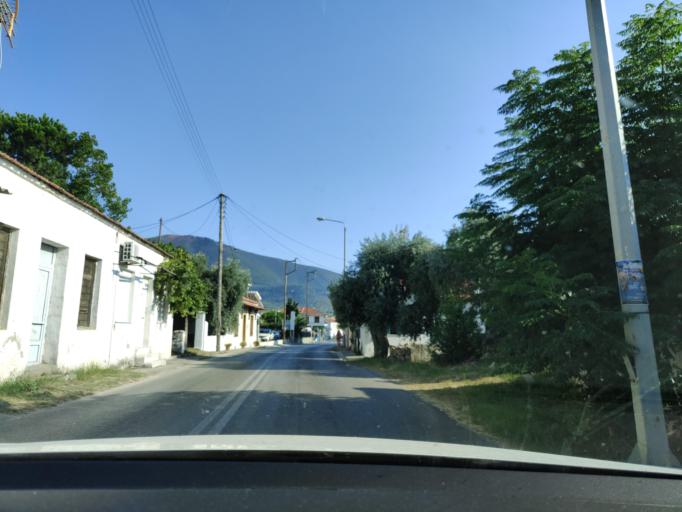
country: GR
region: East Macedonia and Thrace
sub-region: Nomos Kavalas
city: Prinos
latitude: 40.7094
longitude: 24.5341
